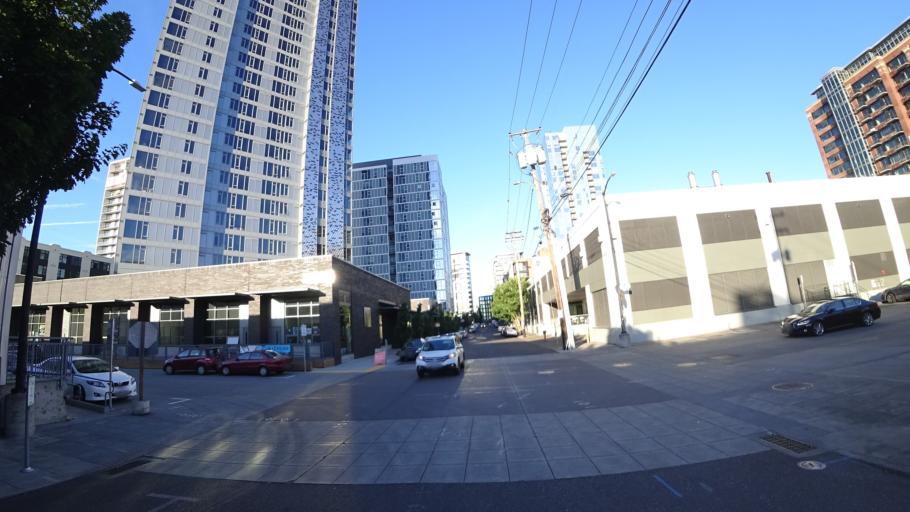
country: US
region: Oregon
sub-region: Multnomah County
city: Portland
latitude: 45.5322
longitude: -122.6847
